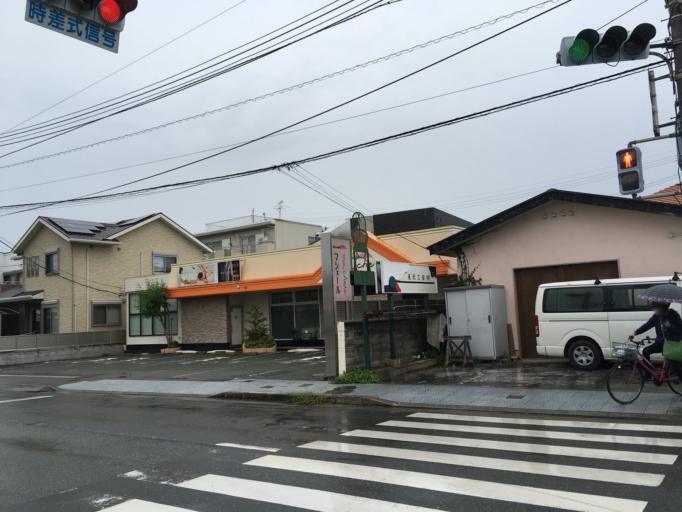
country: JP
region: Kumamoto
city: Kumamoto
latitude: 32.8012
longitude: 130.7301
